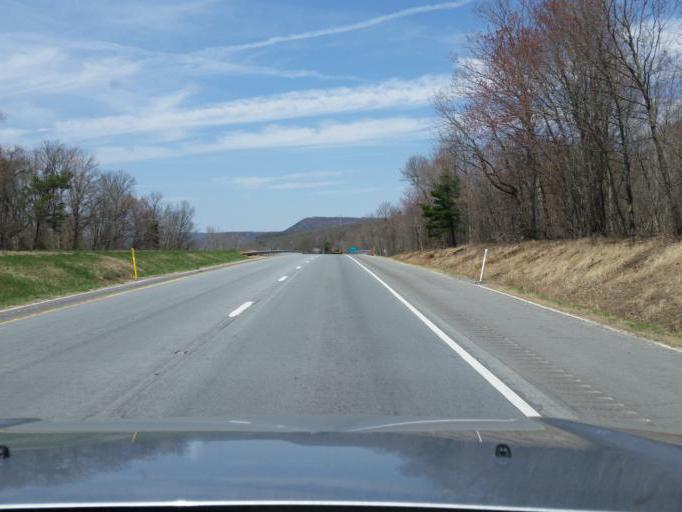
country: US
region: Pennsylvania
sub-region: Perry County
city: Duncannon
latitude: 40.4396
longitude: -77.0143
